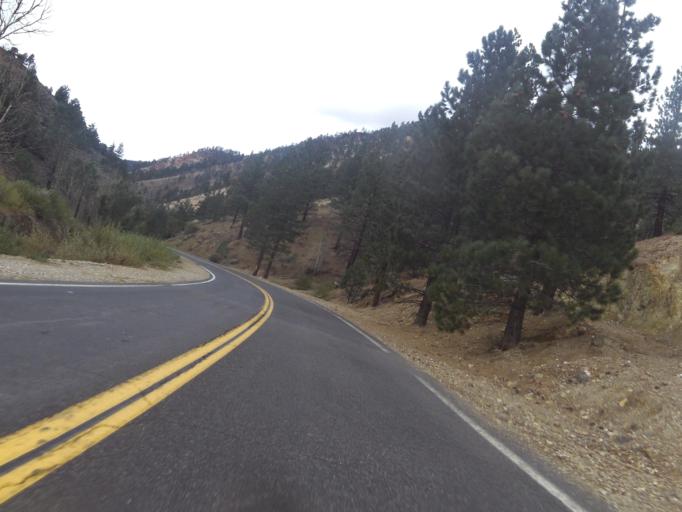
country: US
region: Nevada
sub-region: Douglas County
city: Gardnerville Ranchos
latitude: 38.6659
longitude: -119.6977
